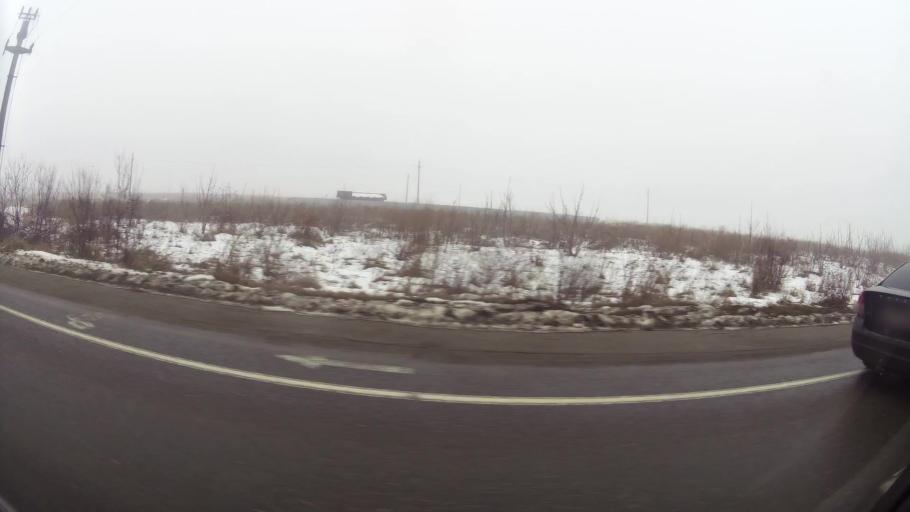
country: RO
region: Ilfov
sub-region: Comuna Chiajna
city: Chiajna
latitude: 44.4522
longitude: 25.9689
